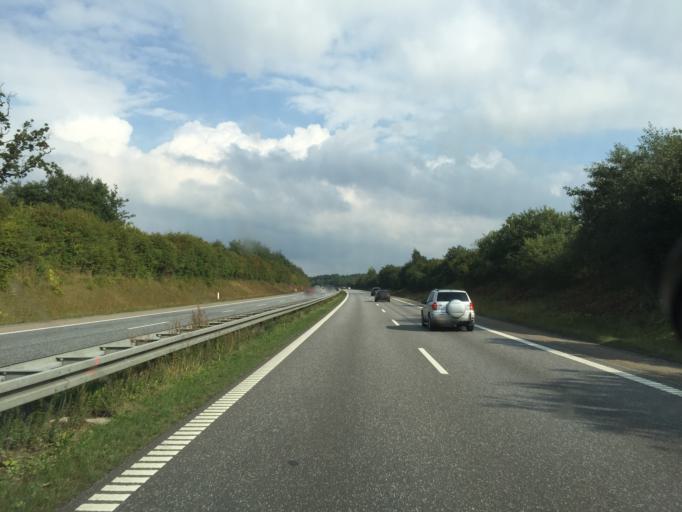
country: DK
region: Zealand
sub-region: Soro Kommune
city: Soro
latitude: 55.4337
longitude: 11.4751
